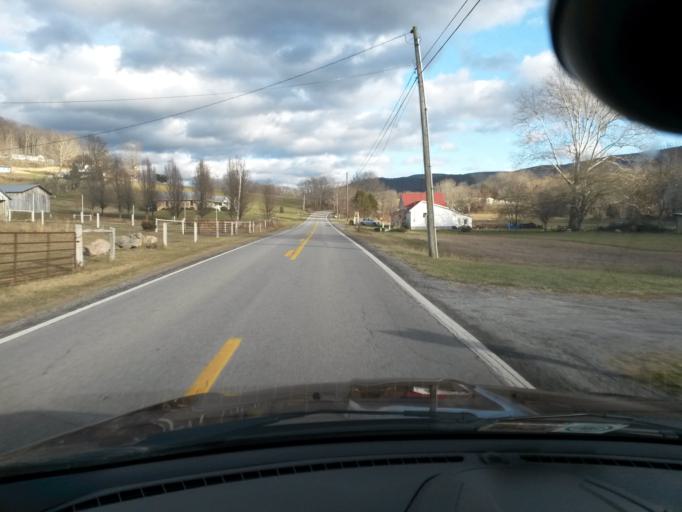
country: US
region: West Virginia
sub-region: Monroe County
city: Union
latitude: 37.4781
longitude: -80.6362
